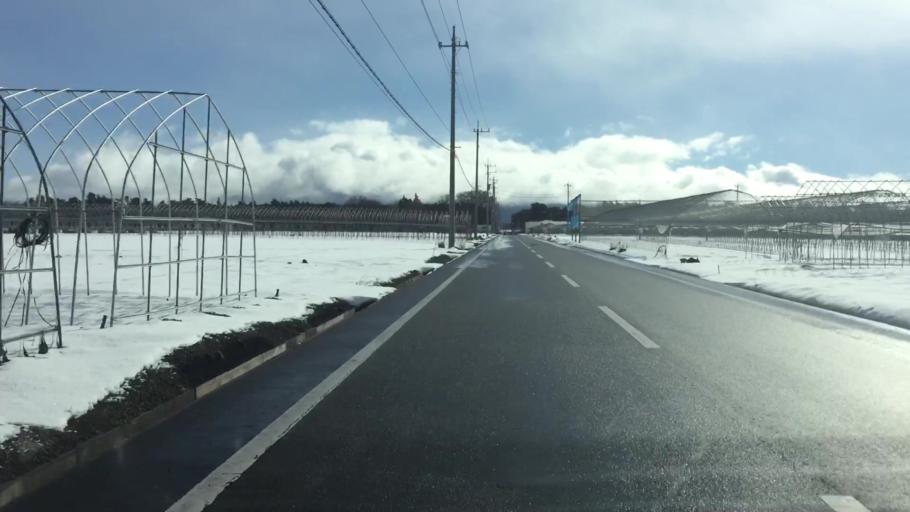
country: JP
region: Gunma
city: Numata
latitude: 36.6301
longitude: 139.0901
